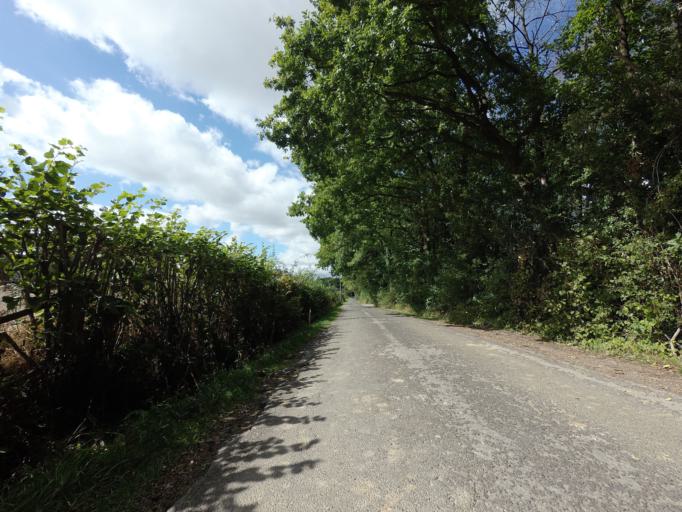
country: GB
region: England
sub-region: Kent
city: Staplehurst
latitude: 51.1326
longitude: 0.5624
